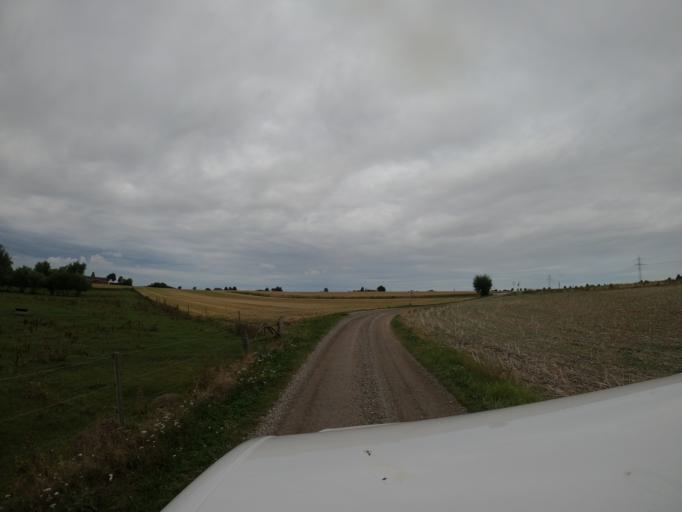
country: SE
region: Skane
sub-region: Kavlinge Kommun
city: Kaevlinge
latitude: 55.7574
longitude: 13.1269
